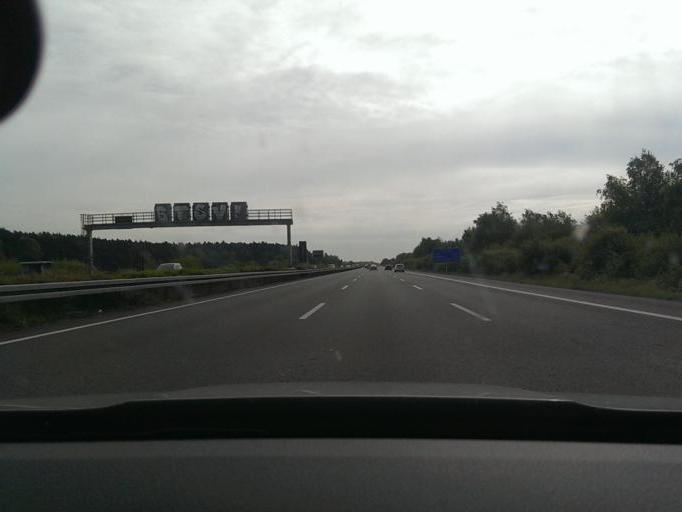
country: DE
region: Lower Saxony
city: Lehre
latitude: 52.3096
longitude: 10.6410
